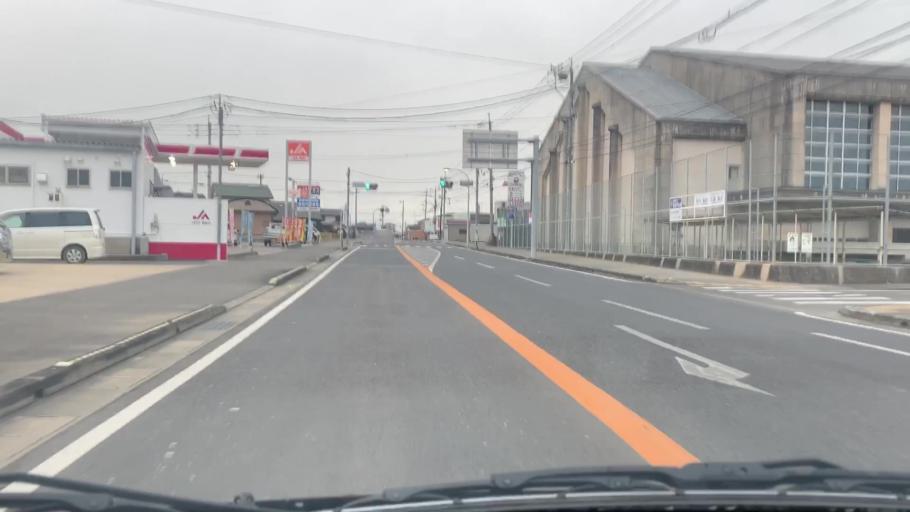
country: JP
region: Saga Prefecture
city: Kashima
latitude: 33.1832
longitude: 130.1908
